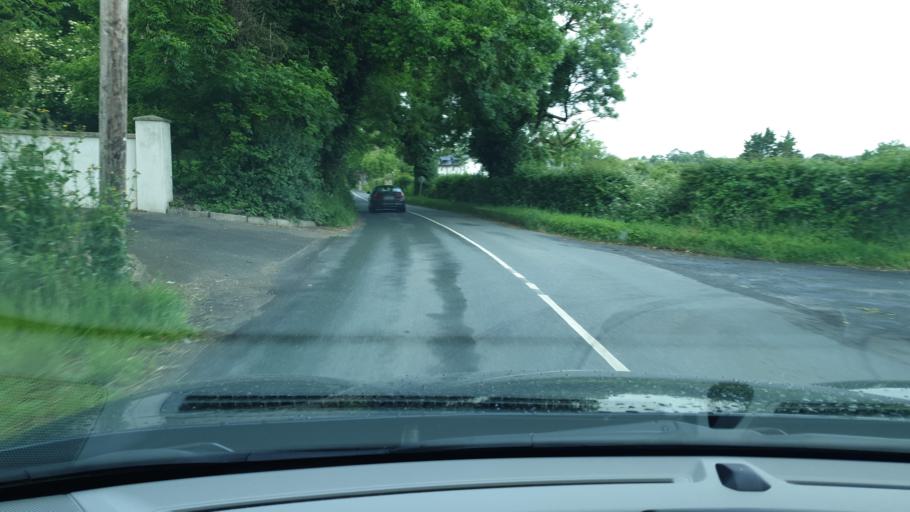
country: IE
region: Leinster
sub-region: An Mhi
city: Ashbourne
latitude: 53.5672
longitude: -6.3718
